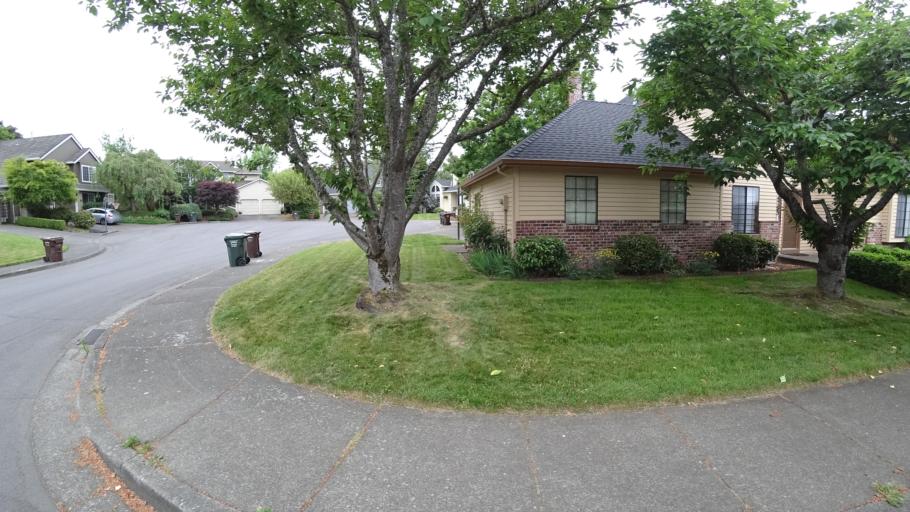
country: US
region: Oregon
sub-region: Washington County
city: Bethany
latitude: 45.5546
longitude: -122.8597
